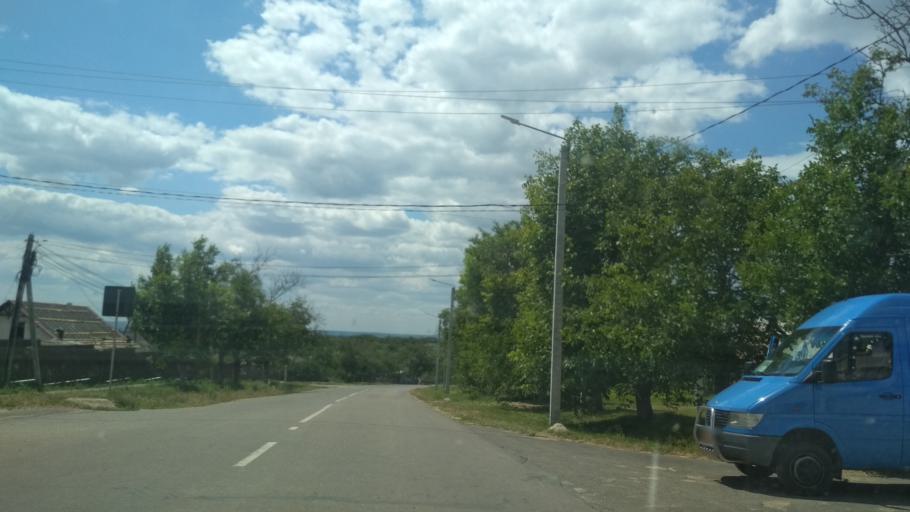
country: MD
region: Criuleni
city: Criuleni
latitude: 47.1779
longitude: 29.2101
